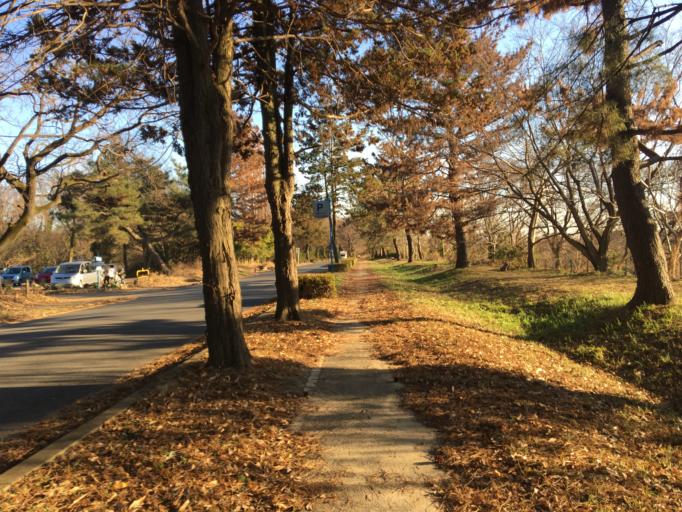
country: JP
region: Saitama
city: Shiki
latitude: 35.8460
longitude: 139.6049
